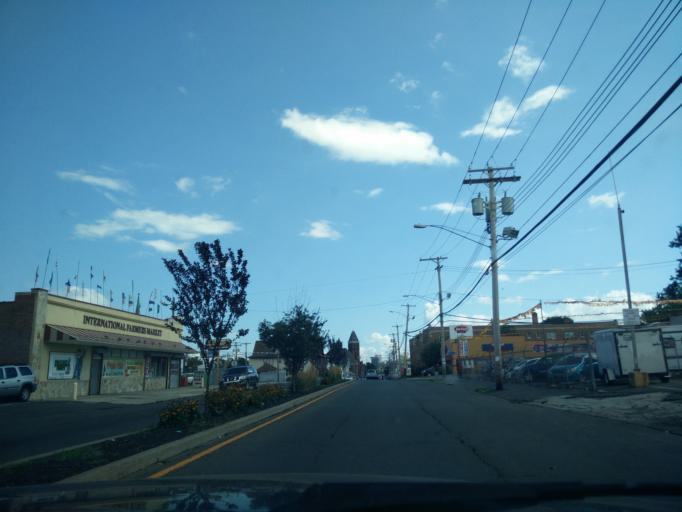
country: US
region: Connecticut
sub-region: Fairfield County
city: Bridgeport
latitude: 41.1946
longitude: -73.1990
